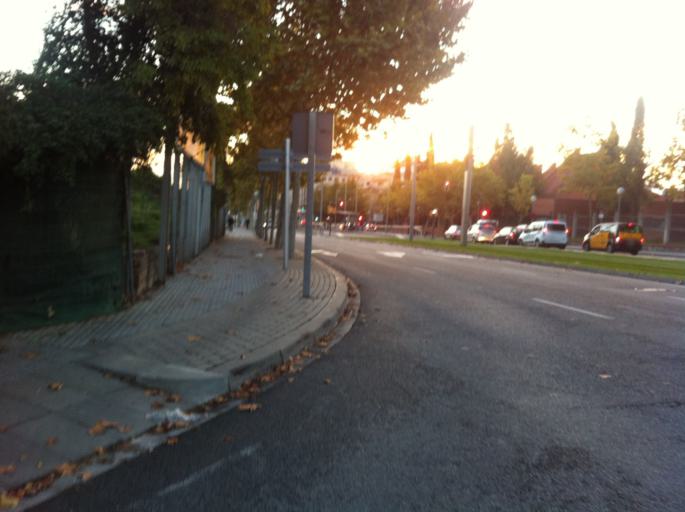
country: ES
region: Catalonia
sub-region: Provincia de Barcelona
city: Esplugues de Llobregat
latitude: 41.3769
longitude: 2.0971
